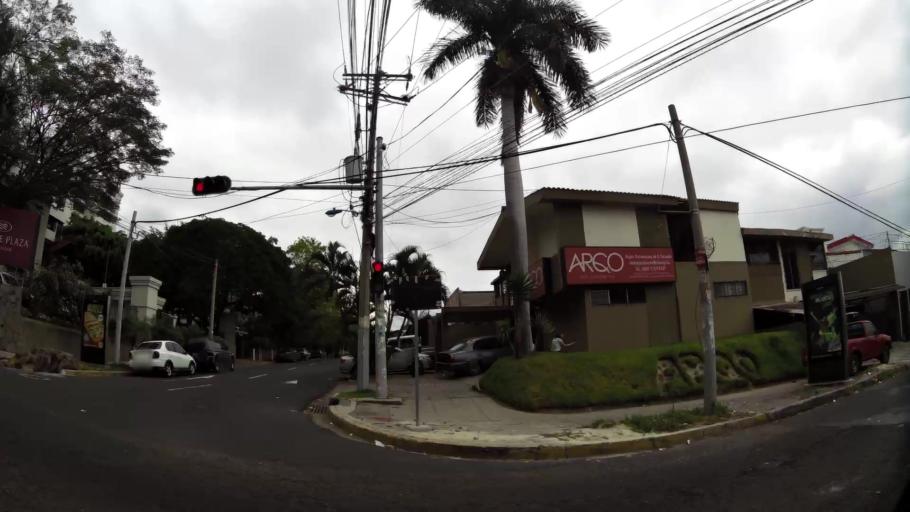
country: SV
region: San Salvador
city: Mejicanos
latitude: 13.7088
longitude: -89.2404
